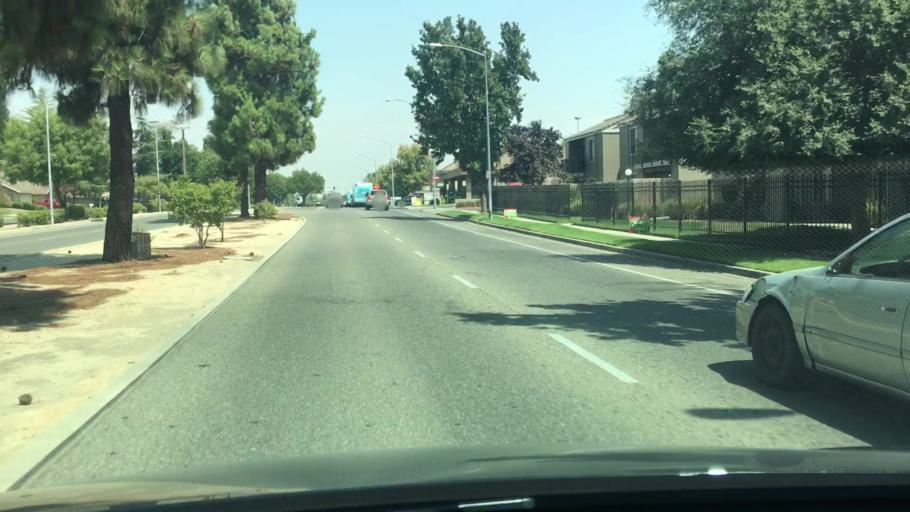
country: US
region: California
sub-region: Fresno County
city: Clovis
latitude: 36.8519
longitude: -119.7781
